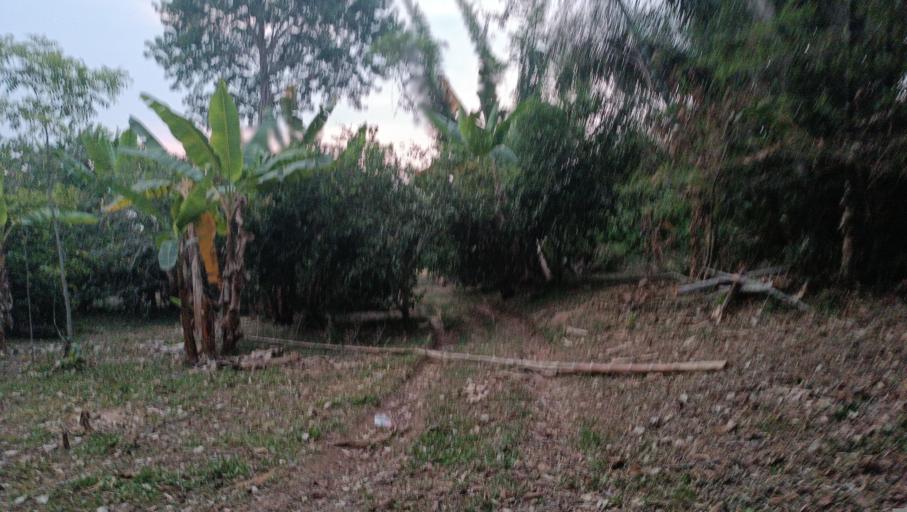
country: BO
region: La Paz
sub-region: Provincia Larecaja
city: Guanay
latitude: -15.5680
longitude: -67.3278
